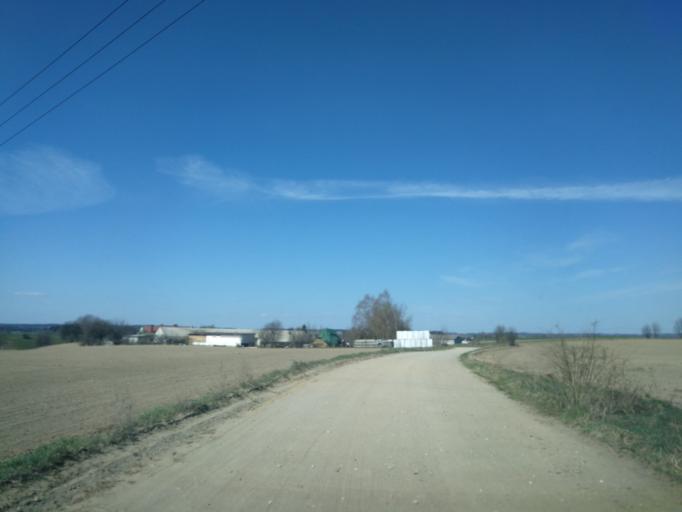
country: PL
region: Warmian-Masurian Voivodeship
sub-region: Powiat dzialdowski
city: Rybno
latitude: 53.4357
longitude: 19.9628
